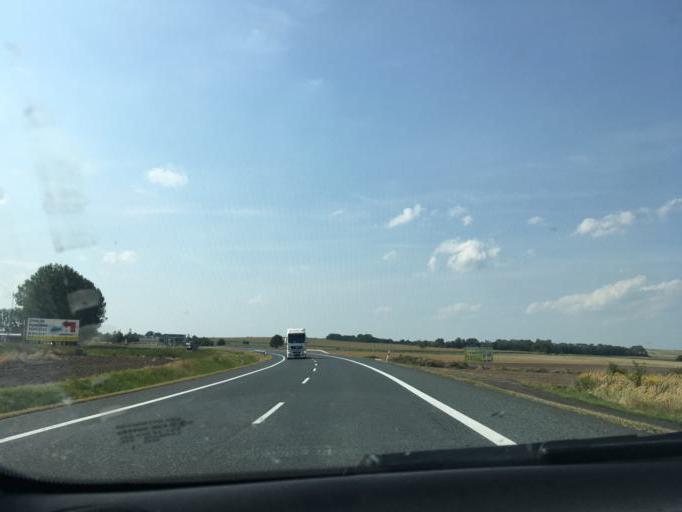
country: PL
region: Opole Voivodeship
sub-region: Powiat prudnicki
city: Prudnik
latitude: 50.3332
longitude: 17.5949
